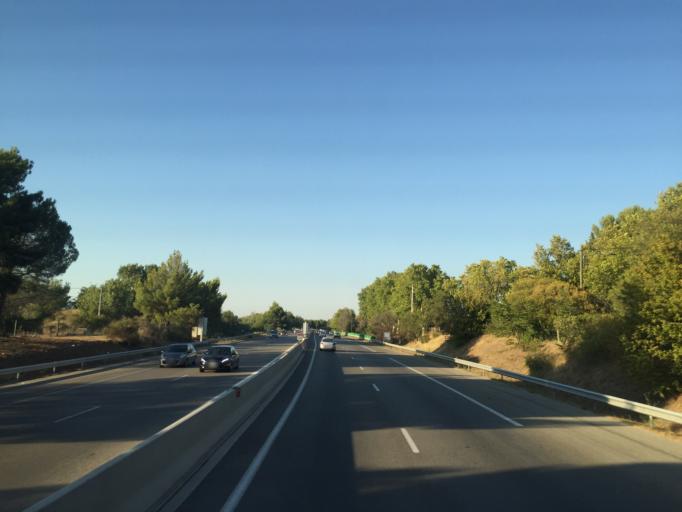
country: FR
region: Provence-Alpes-Cote d'Azur
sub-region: Departement des Bouches-du-Rhone
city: Venelles
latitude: 43.5661
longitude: 5.4644
